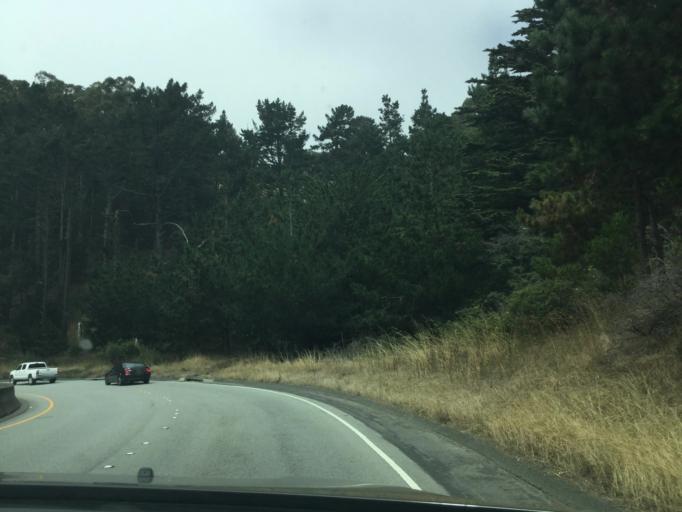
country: US
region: California
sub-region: San Mateo County
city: Pacifica
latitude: 37.6260
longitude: -122.4853
